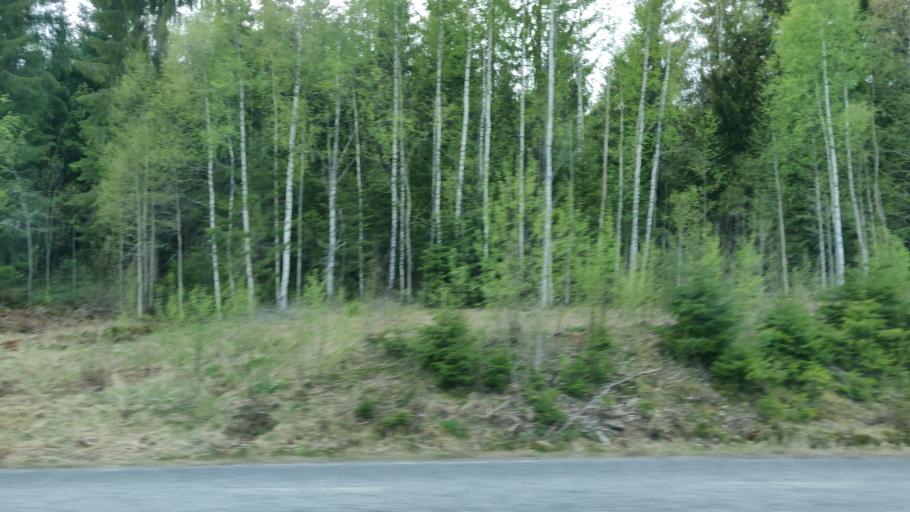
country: SE
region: Vaermland
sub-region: Munkfors Kommun
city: Munkfors
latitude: 59.7608
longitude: 13.4421
